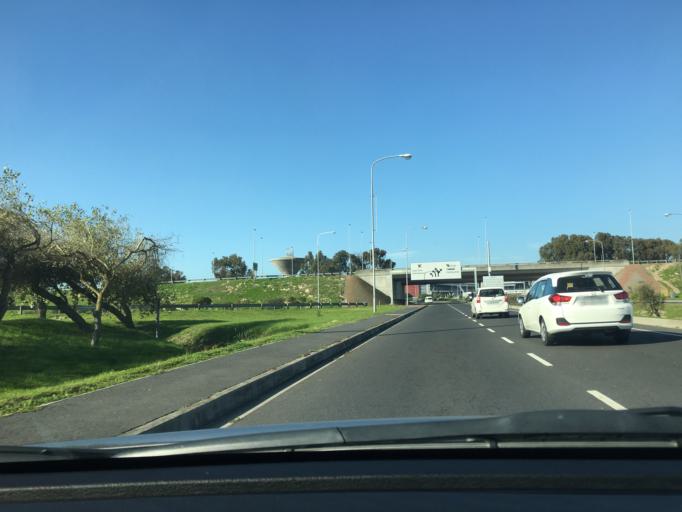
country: ZA
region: Western Cape
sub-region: City of Cape Town
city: Lansdowne
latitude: -33.9684
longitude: 18.5882
